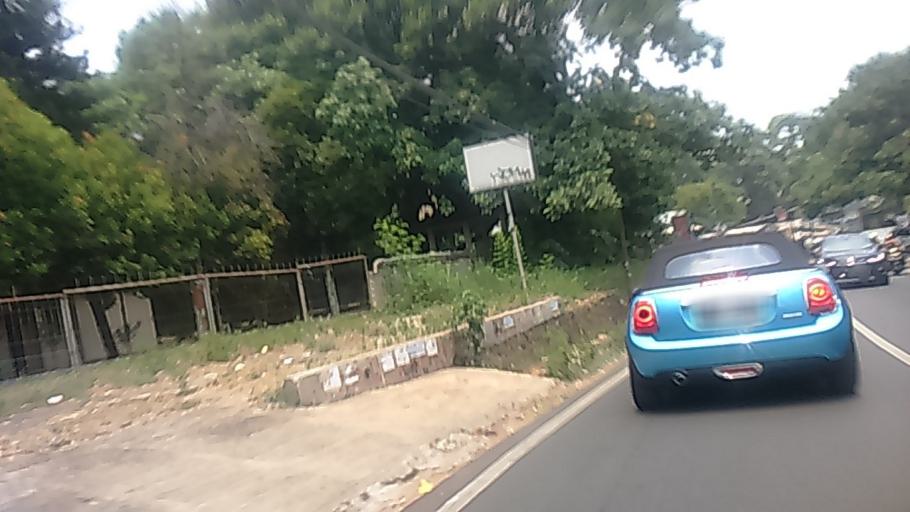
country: ID
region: West Java
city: Pamulang
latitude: -6.3013
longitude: 106.7739
